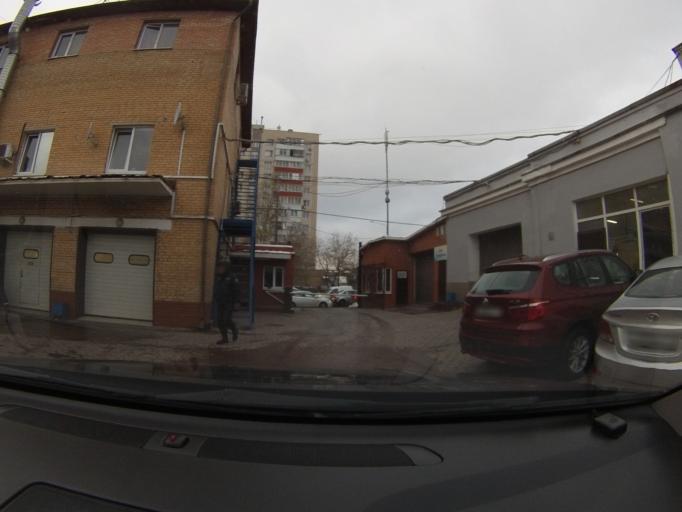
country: RU
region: Moscow
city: Lefortovo
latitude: 55.7325
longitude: 37.7121
